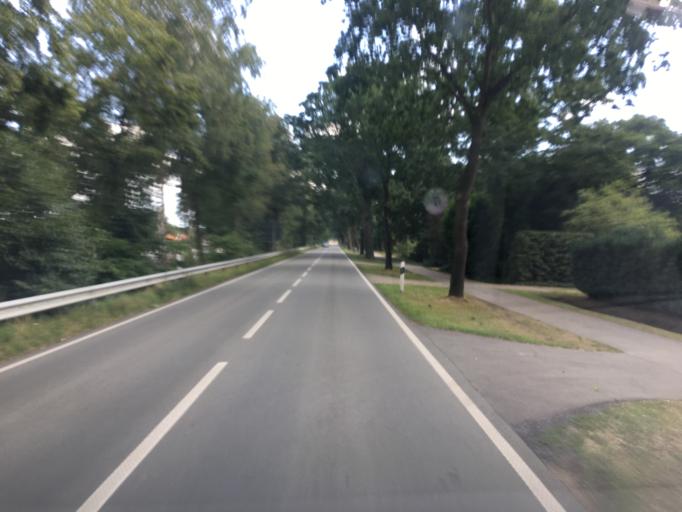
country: DE
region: Lower Saxony
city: Friesoythe
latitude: 53.0907
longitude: 7.7925
